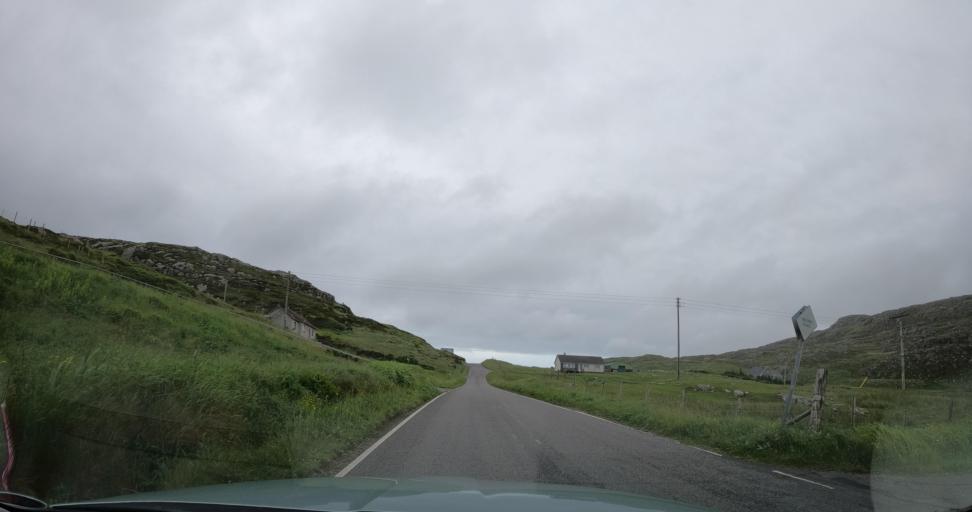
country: GB
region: Scotland
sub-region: Eilean Siar
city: Barra
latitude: 56.9607
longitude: -7.5064
